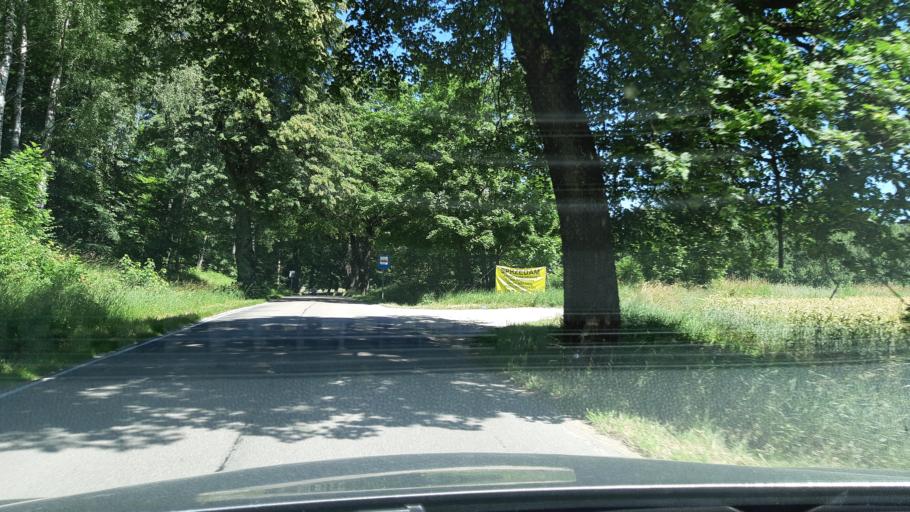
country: PL
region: Warmian-Masurian Voivodeship
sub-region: Powiat gizycki
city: Ryn
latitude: 53.9062
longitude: 21.6721
